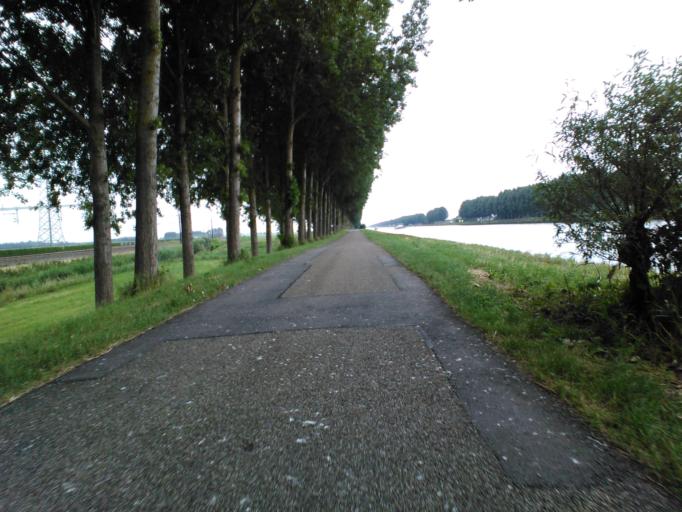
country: NL
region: Utrecht
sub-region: Stichtse Vecht
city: Vreeland
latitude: 52.2364
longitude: 5.0086
